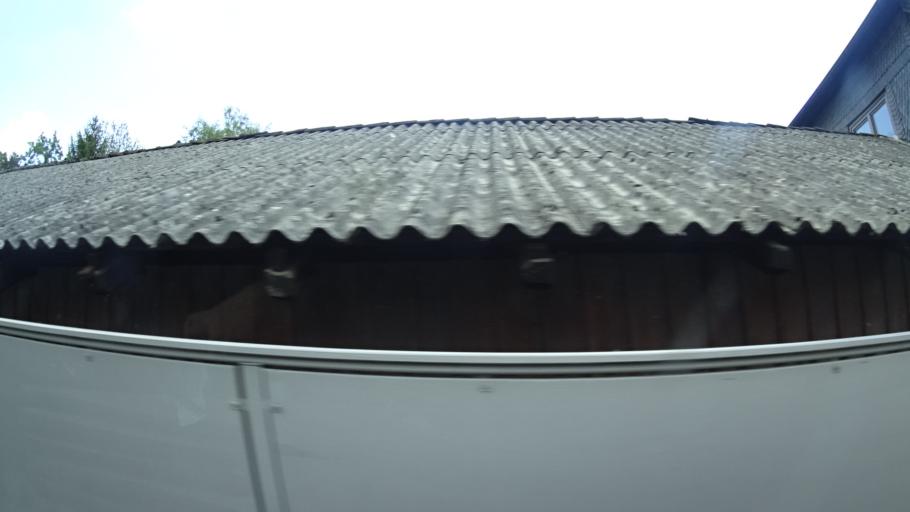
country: DE
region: Thuringia
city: Vachdorf
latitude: 50.5287
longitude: 10.5374
